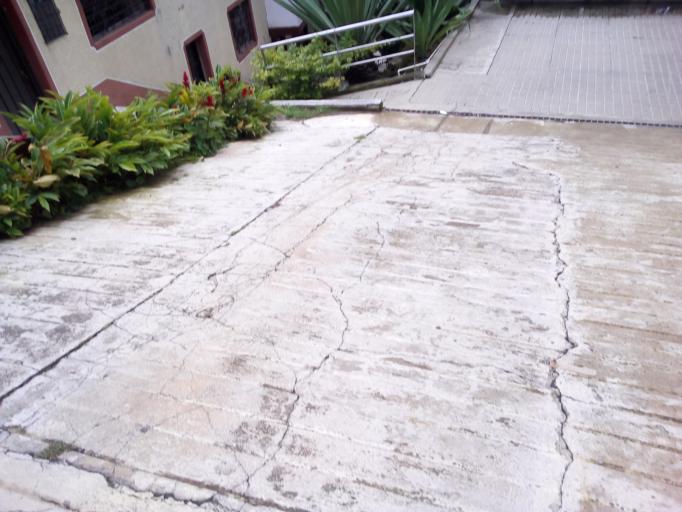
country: CO
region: Tolima
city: Ibague
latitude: 4.4470
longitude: -75.2430
